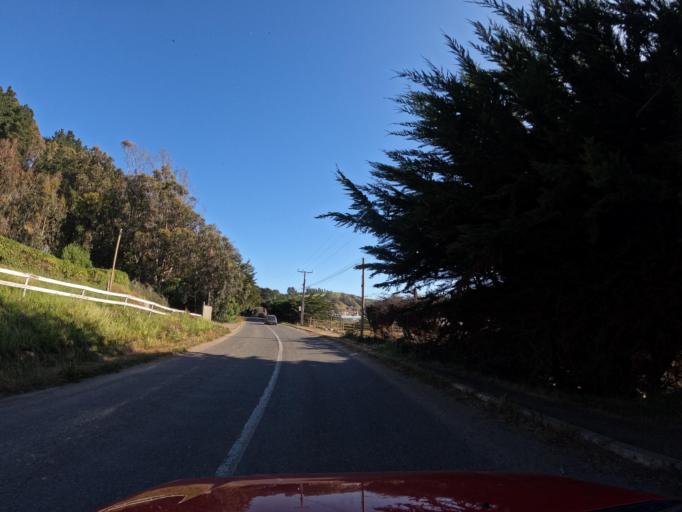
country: CL
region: Maule
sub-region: Provincia de Talca
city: Constitucion
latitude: -34.8779
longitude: -72.1553
